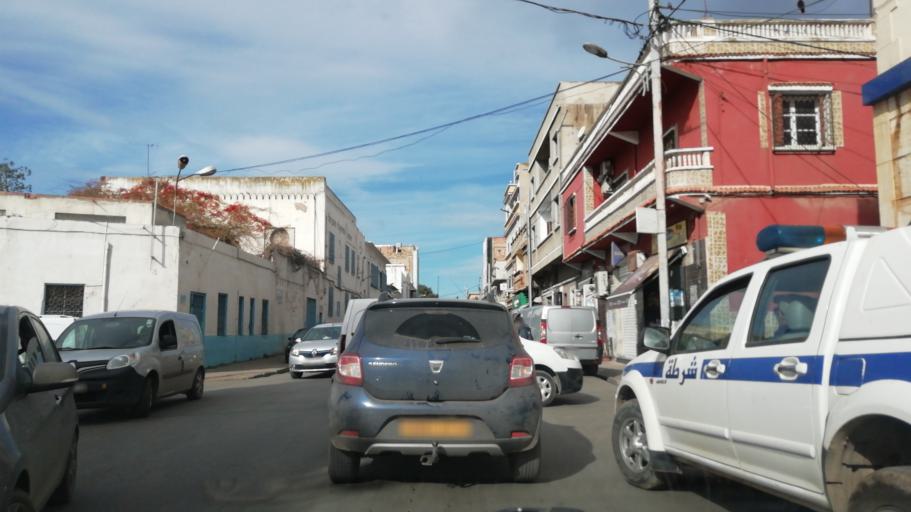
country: DZ
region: Oran
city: Oran
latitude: 35.6929
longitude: -0.6304
